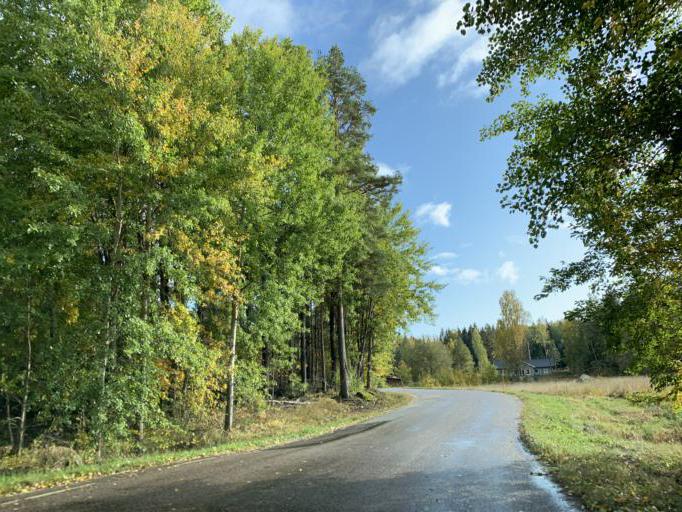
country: SE
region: Soedermanland
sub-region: Eskilstuna Kommun
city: Kvicksund
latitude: 59.3306
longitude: 16.2553
